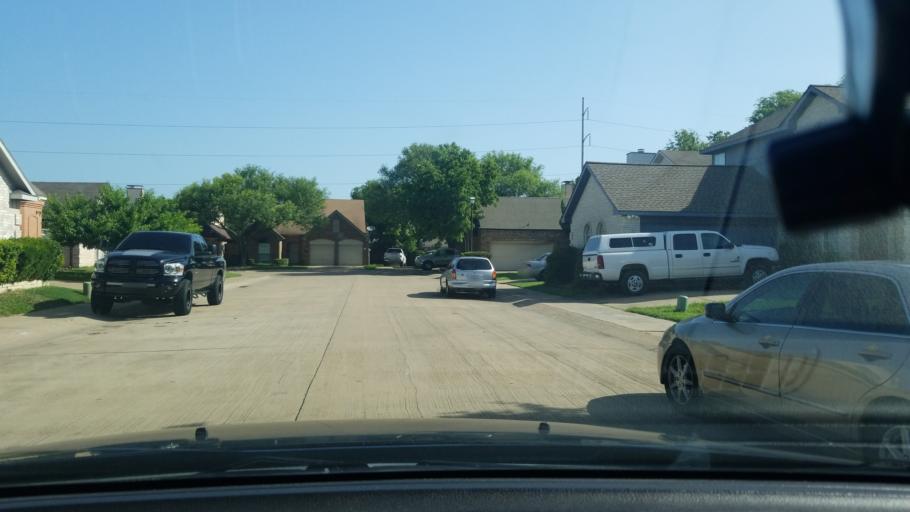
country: US
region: Texas
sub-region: Dallas County
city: Mesquite
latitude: 32.8061
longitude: -96.6780
